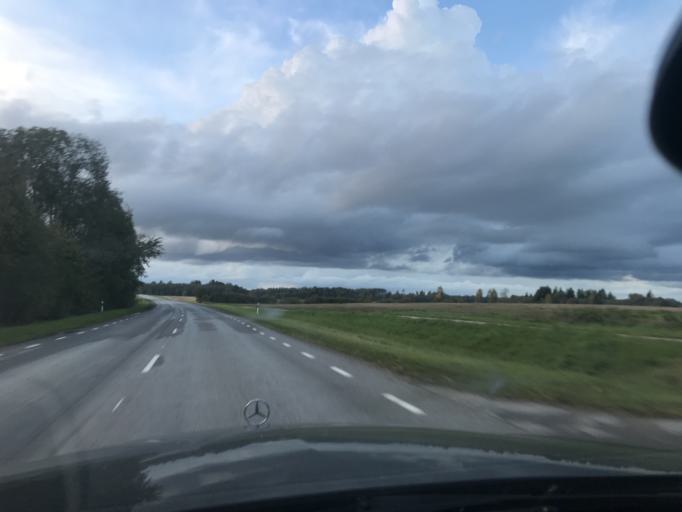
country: EE
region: Vorumaa
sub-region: Antsla vald
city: Vana-Antsla
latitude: 57.9395
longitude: 26.3090
